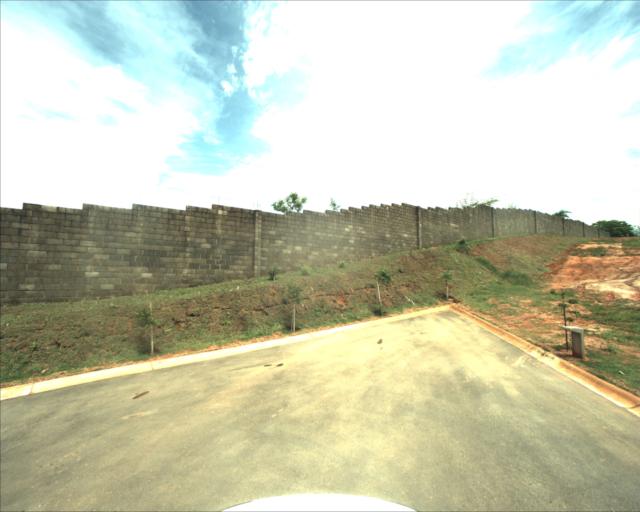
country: BR
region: Sao Paulo
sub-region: Votorantim
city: Votorantim
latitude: -23.5757
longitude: -47.5068
